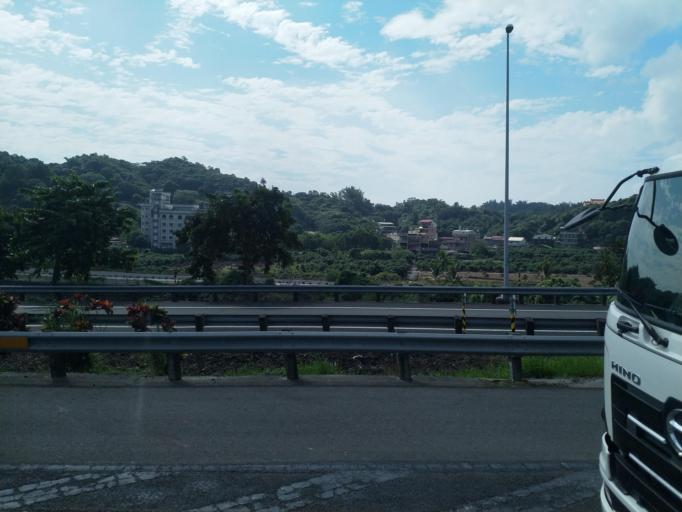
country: TW
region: Taiwan
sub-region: Pingtung
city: Pingtung
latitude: 22.7968
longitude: 120.4513
